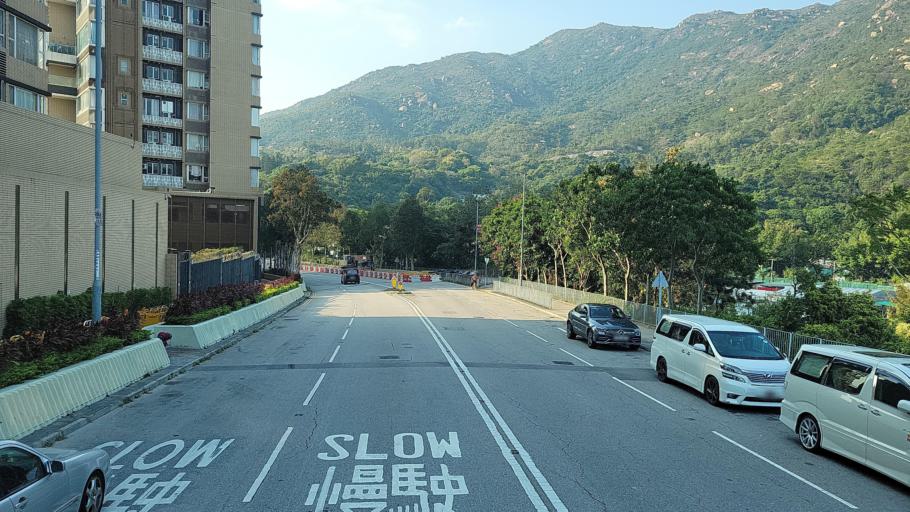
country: HK
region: Tuen Mun
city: Tuen Mun
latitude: 22.3749
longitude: 114.0018
